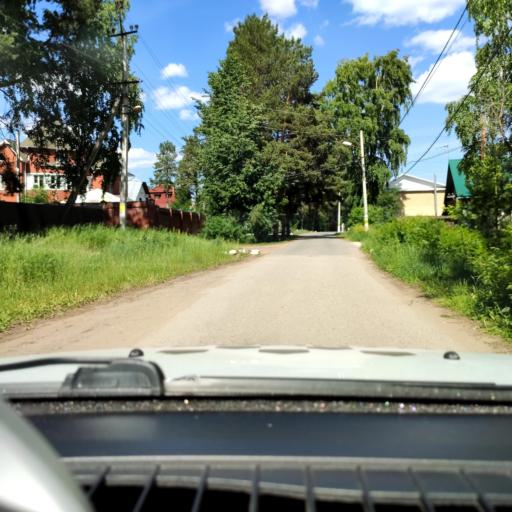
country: RU
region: Perm
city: Perm
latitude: 58.0564
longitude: 56.3043
